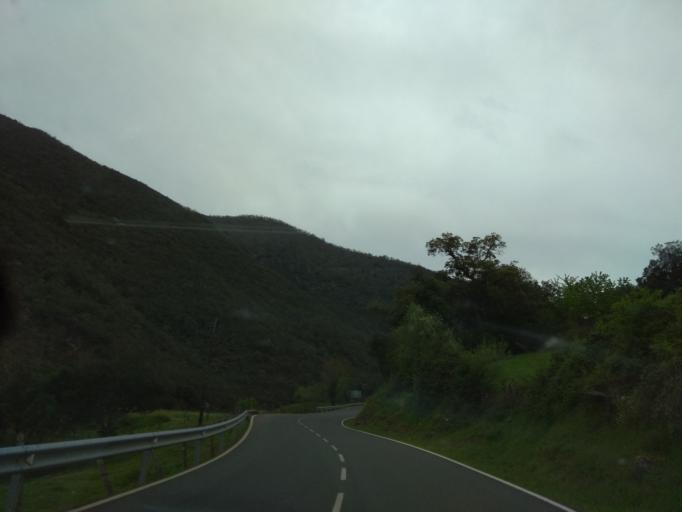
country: ES
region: Cantabria
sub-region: Provincia de Cantabria
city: Potes
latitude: 43.1080
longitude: -4.6419
